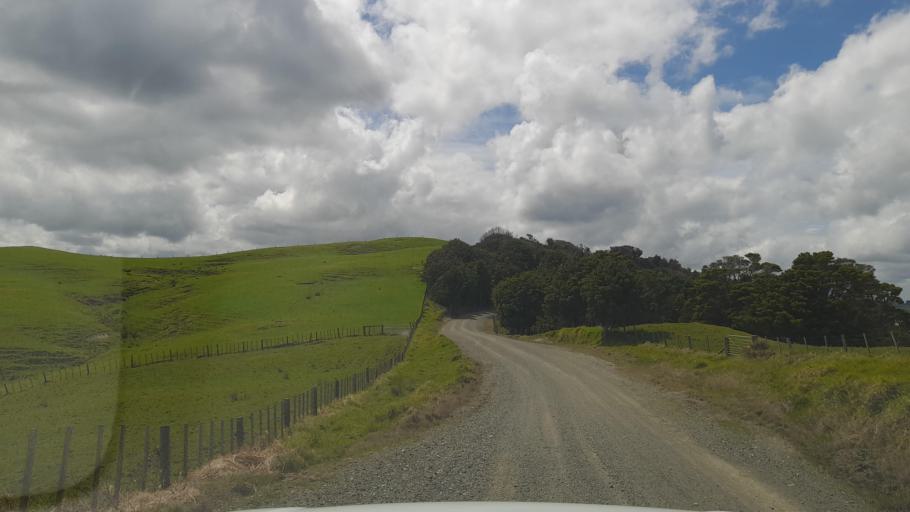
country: NZ
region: Auckland
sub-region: Auckland
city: Wellsford
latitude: -36.2119
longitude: 174.3279
